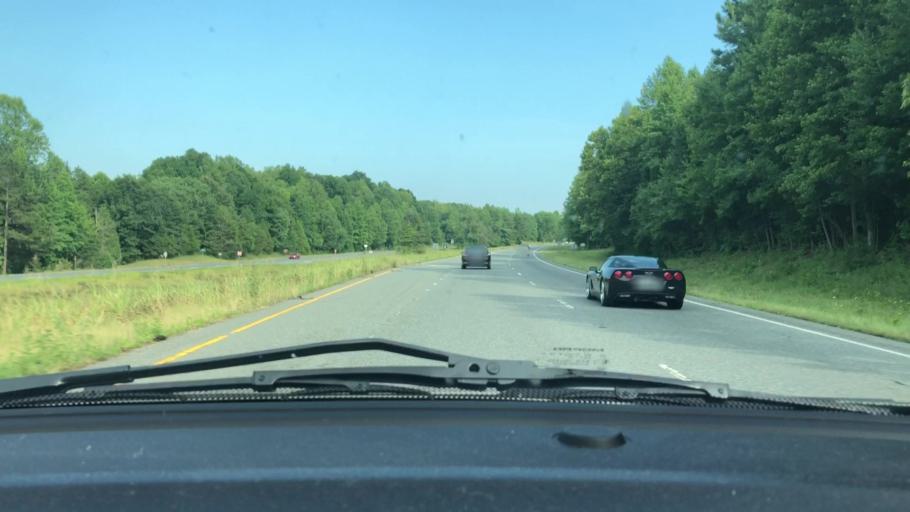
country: US
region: North Carolina
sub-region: Randolph County
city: Liberty
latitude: 35.8841
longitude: -79.6400
